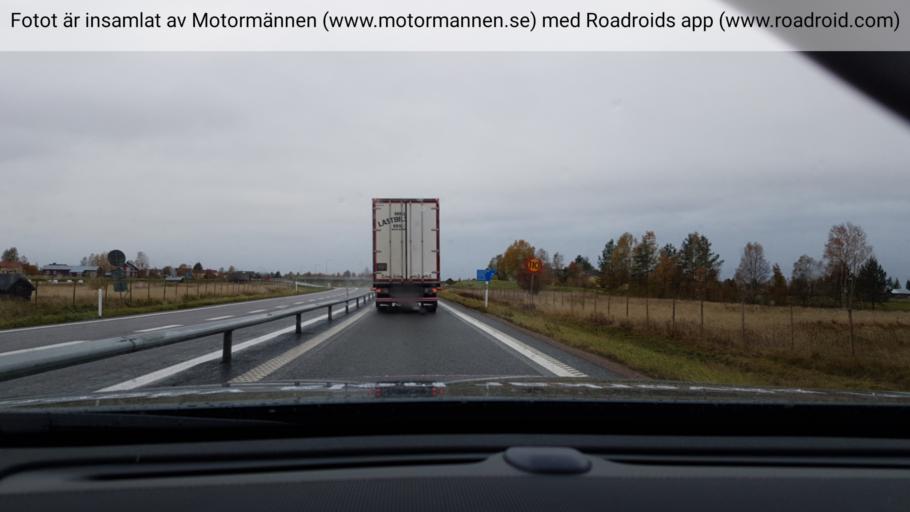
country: SE
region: Norrbotten
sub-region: Pitea Kommun
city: Rosvik
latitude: 65.5343
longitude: 21.7986
